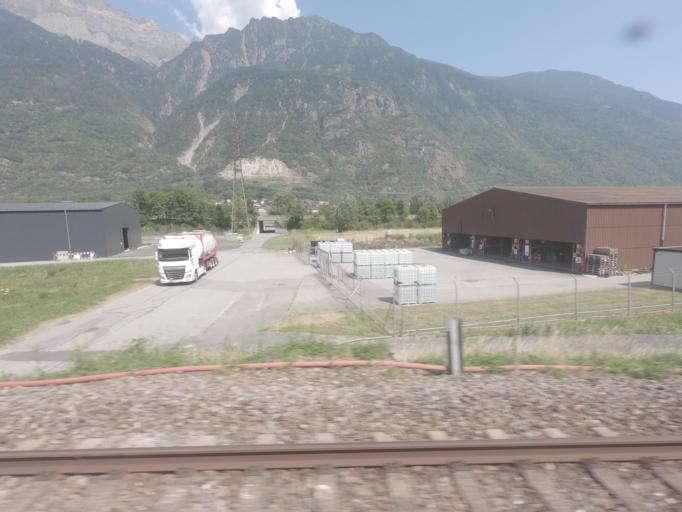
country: CH
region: Valais
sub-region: Martigny District
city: Evionnaz
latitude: 46.1733
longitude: 7.0244
